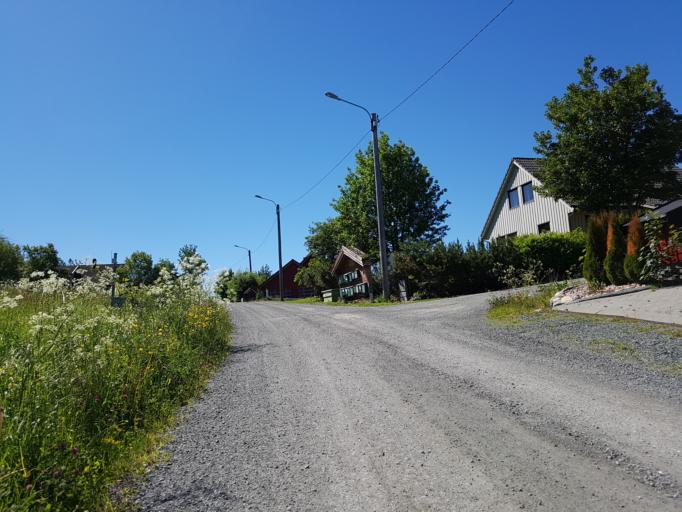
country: NO
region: Sor-Trondelag
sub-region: Skaun
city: Borsa
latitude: 63.4330
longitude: 10.1851
